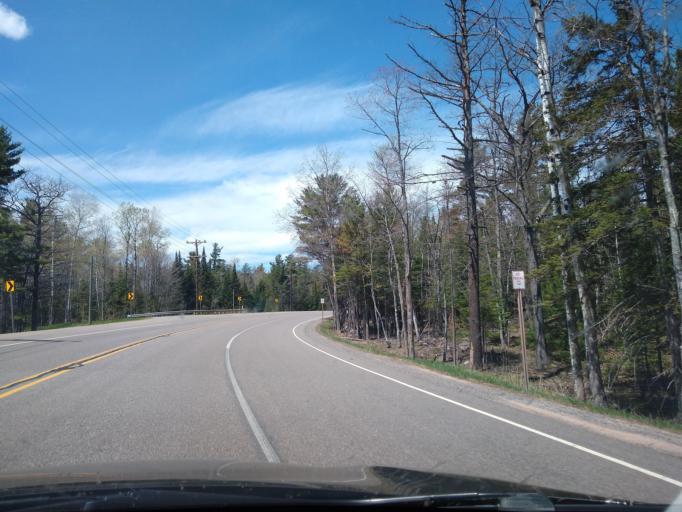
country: US
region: Michigan
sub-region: Marquette County
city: Trowbridge Park
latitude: 46.6066
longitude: -87.4670
